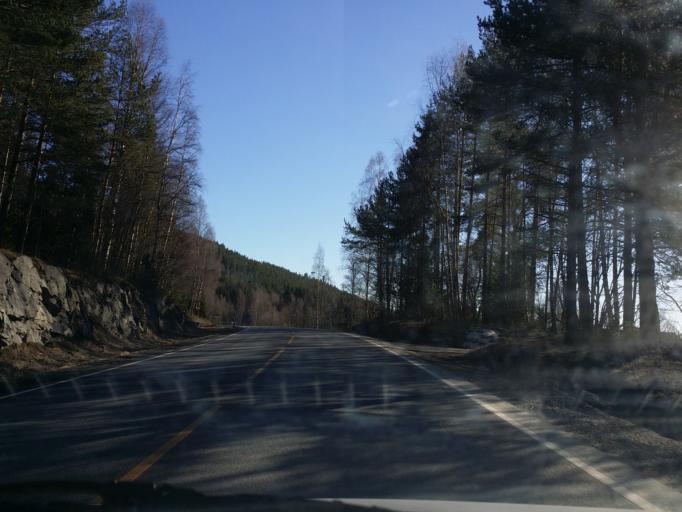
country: NO
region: Buskerud
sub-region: Ringerike
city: Honefoss
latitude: 60.2651
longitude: 10.1858
